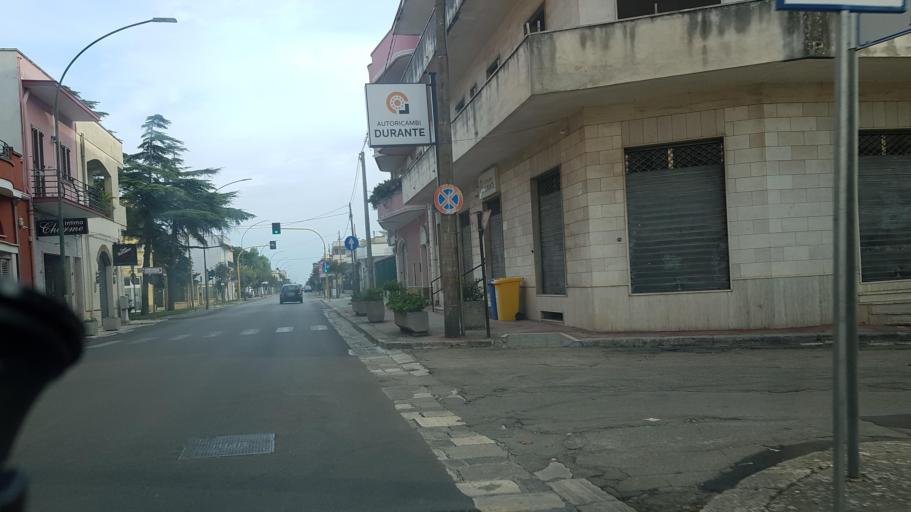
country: IT
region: Apulia
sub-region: Provincia di Lecce
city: Trepuzzi
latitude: 40.4029
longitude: 18.0750
